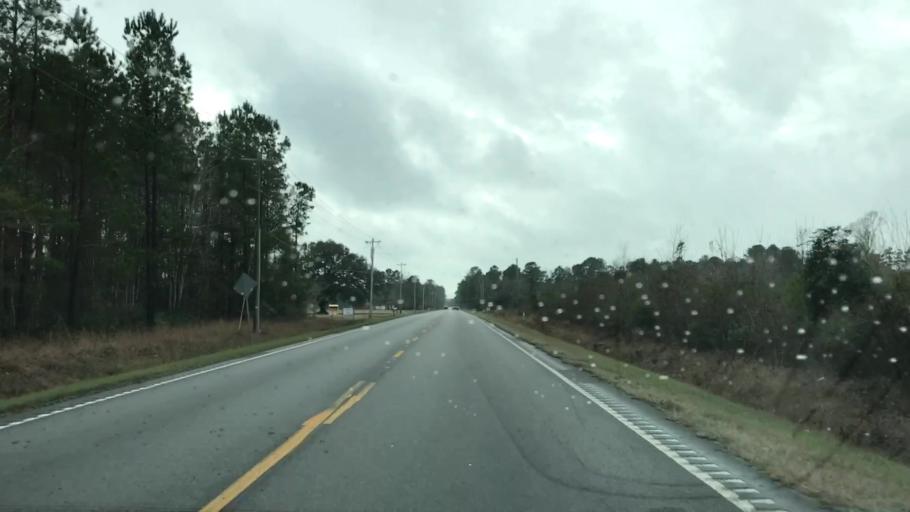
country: US
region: South Carolina
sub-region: Horry County
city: Socastee
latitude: 33.7379
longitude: -79.0813
